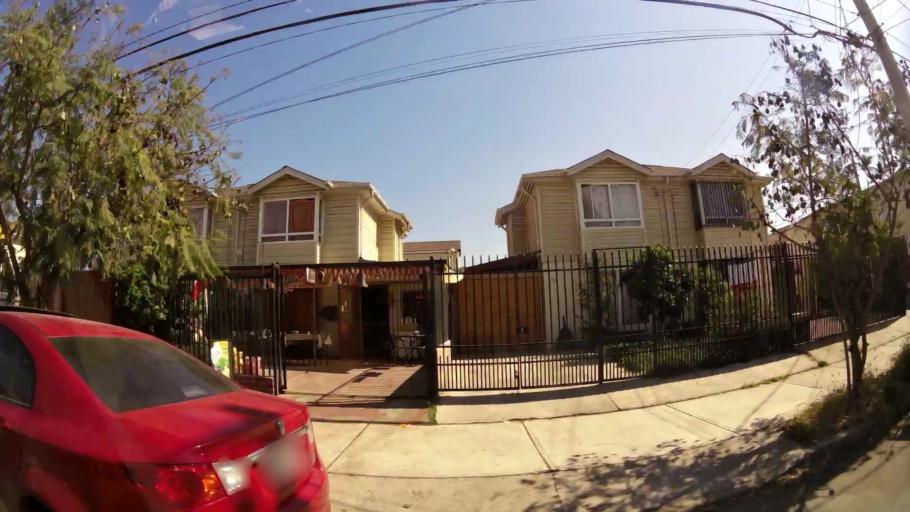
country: CL
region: Santiago Metropolitan
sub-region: Provincia de Talagante
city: Penaflor
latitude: -33.5643
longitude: -70.8224
